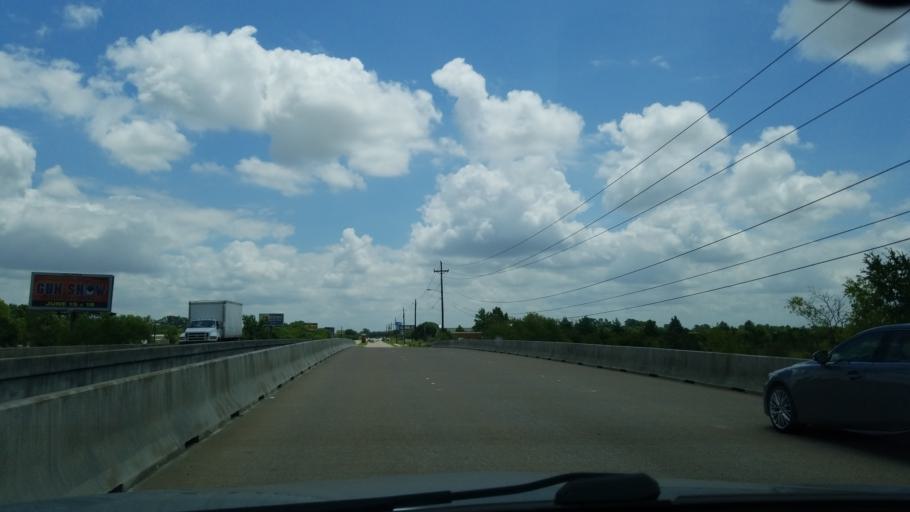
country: US
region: Texas
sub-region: Dallas County
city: Farmers Branch
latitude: 32.9514
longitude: -96.9465
